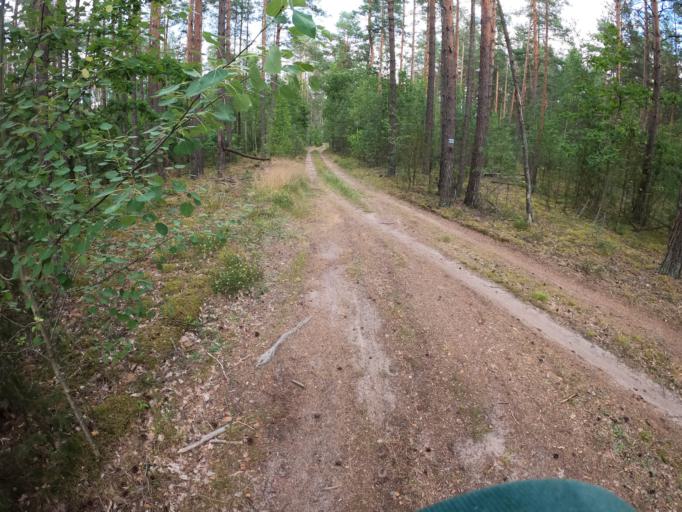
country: LT
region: Alytaus apskritis
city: Druskininkai
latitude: 54.1367
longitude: 24.1734
